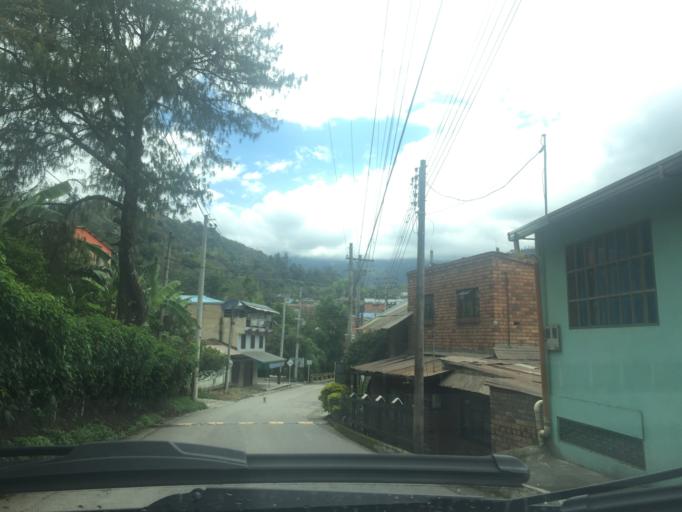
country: CO
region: Cundinamarca
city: San Francisco
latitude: 4.9778
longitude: -74.2898
